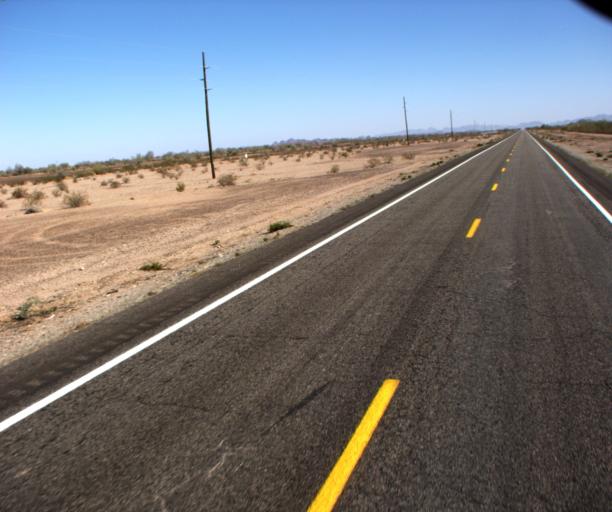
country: US
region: Arizona
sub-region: Yuma County
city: Fortuna Foothills
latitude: 32.8709
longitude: -114.3534
